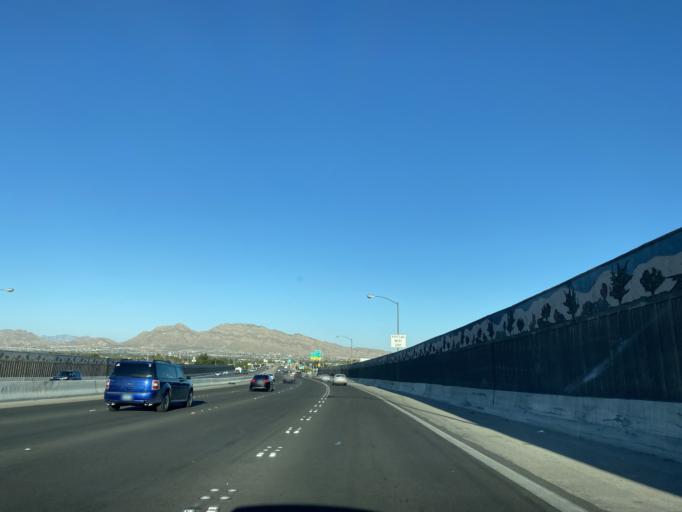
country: US
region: Nevada
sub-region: Clark County
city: Las Vegas
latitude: 36.1674
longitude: -115.1240
